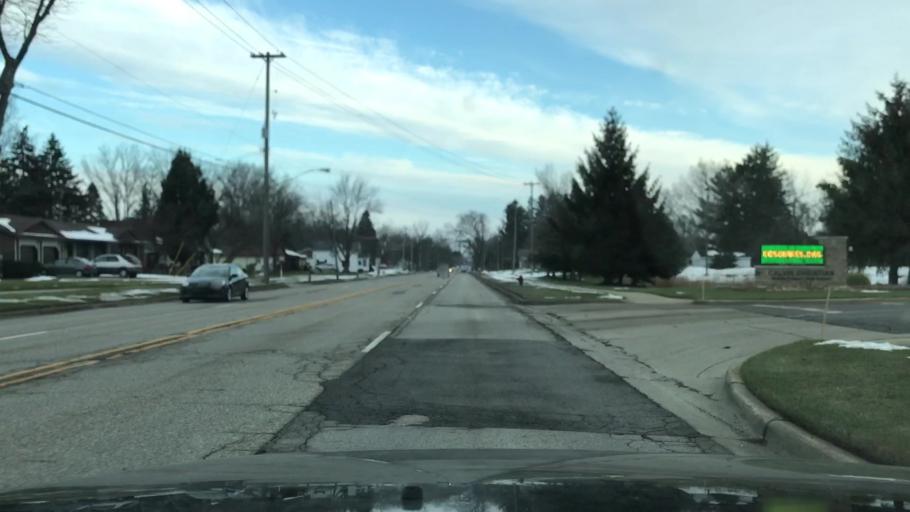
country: US
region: Michigan
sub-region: Kent County
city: Grandville
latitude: 42.8963
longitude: -85.7437
